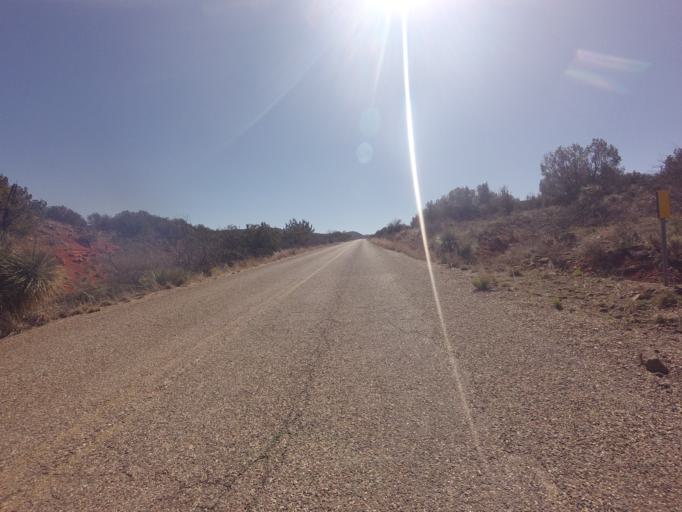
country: US
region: Arizona
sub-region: Yavapai County
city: Lake Montezuma
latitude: 34.6781
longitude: -111.7215
